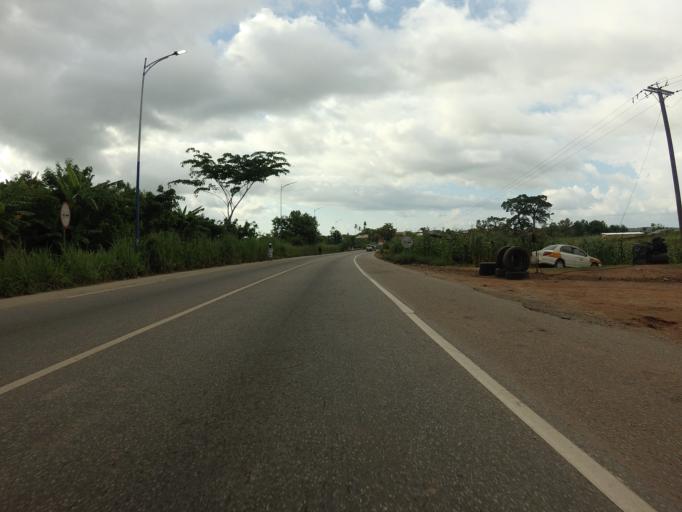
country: GH
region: Ashanti
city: Tafo
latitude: 6.8103
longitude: -1.6490
